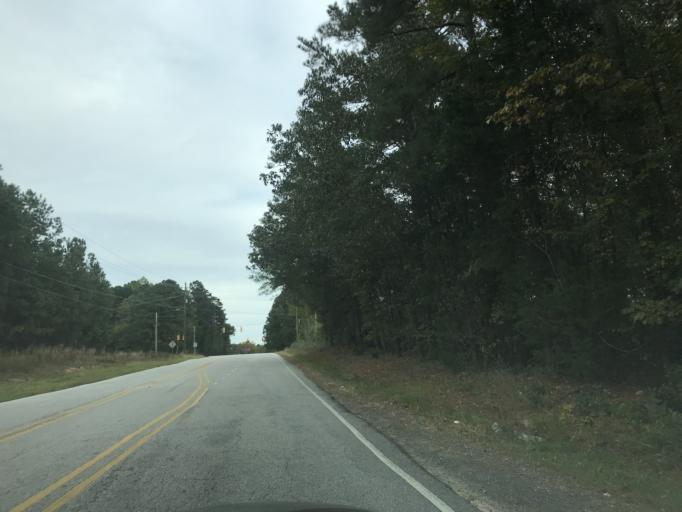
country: US
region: North Carolina
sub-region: Wake County
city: Knightdale
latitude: 35.8436
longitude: -78.5147
